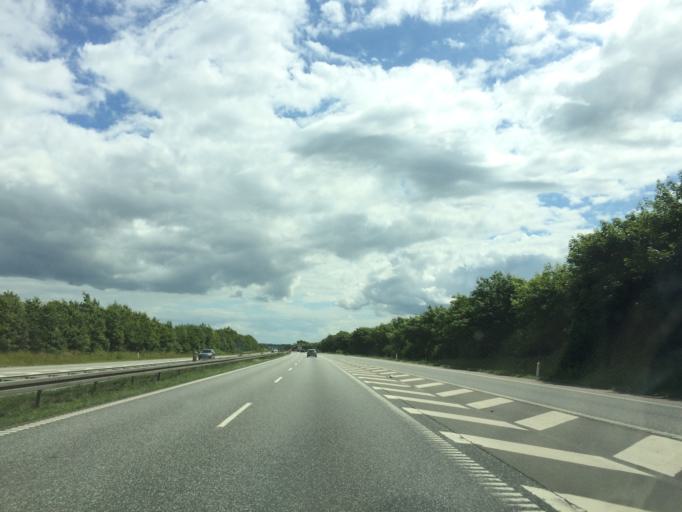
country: DK
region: North Denmark
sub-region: Mariagerfjord Kommune
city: Hobro
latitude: 56.7315
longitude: 9.7068
